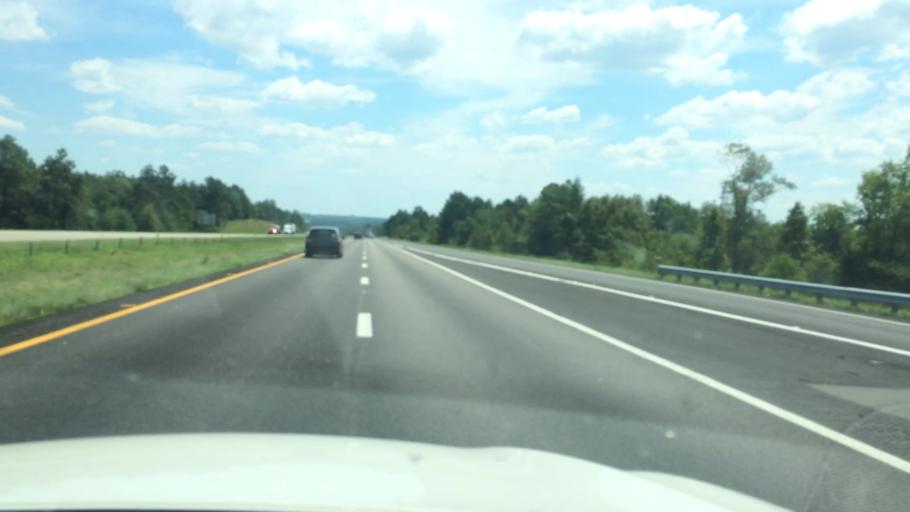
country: US
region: South Carolina
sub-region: Aiken County
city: Aiken
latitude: 33.6404
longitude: -81.7369
